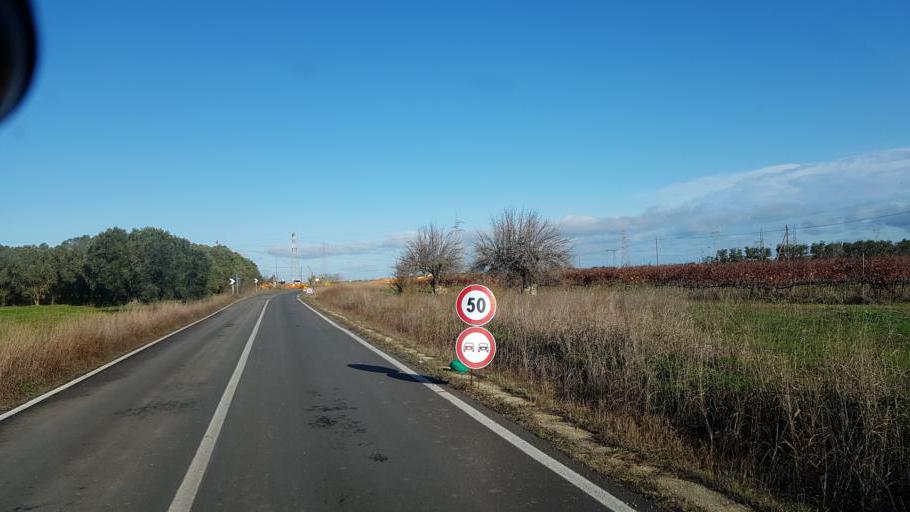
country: IT
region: Apulia
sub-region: Provincia di Brindisi
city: Tuturano
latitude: 40.5511
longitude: 17.9470
